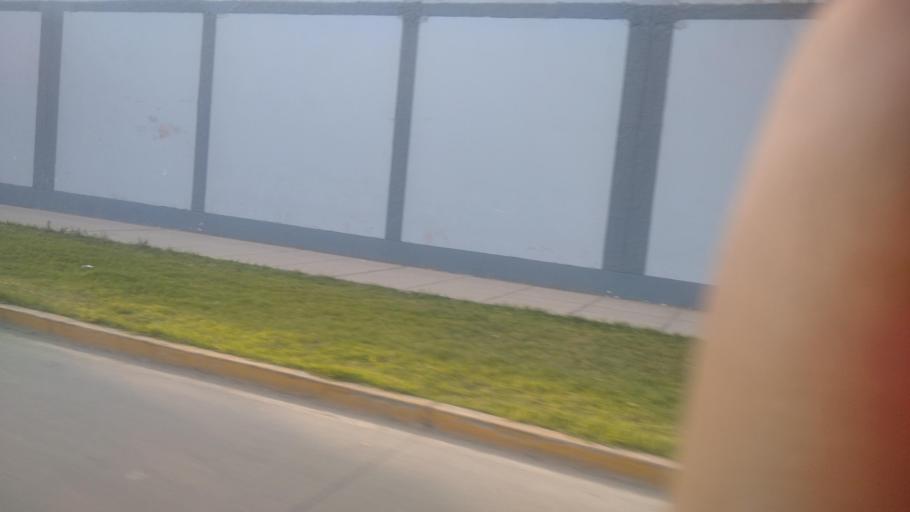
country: PE
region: Lima
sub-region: Lima
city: Vitarte
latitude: -12.0214
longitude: -76.9611
